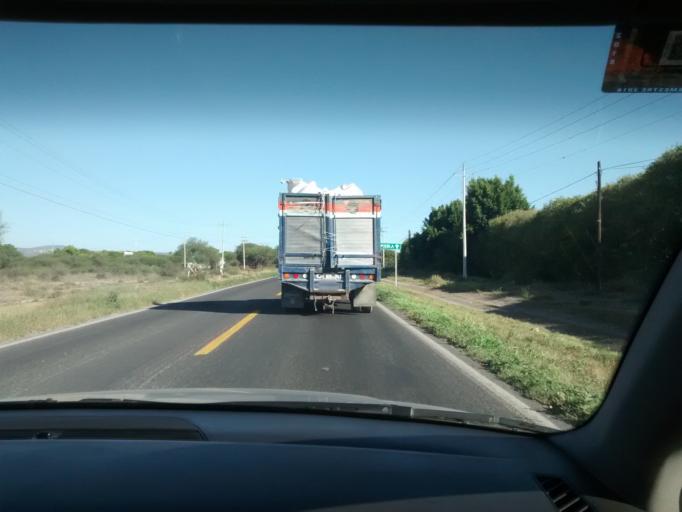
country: MX
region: Puebla
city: San Bartolo Teontepec
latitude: 18.5304
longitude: -97.5213
